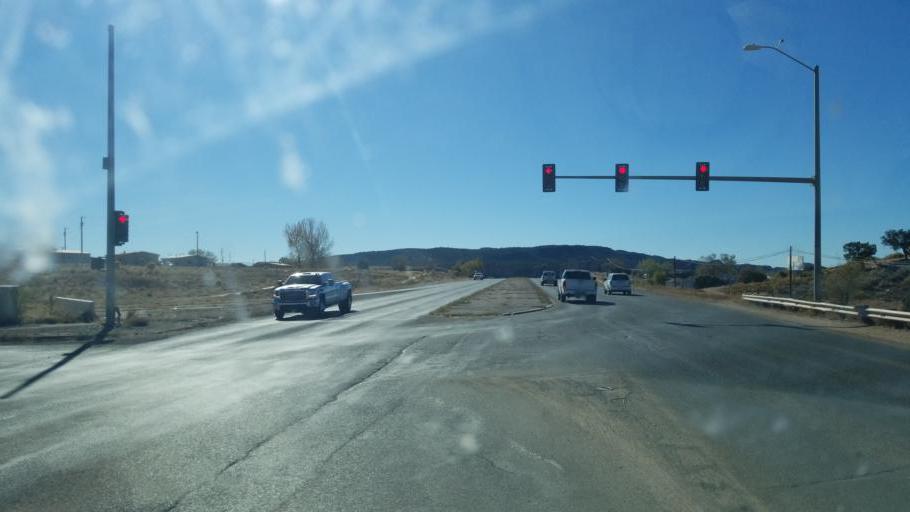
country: US
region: Arizona
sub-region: Apache County
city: Window Rock
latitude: 35.6713
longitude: -109.0594
